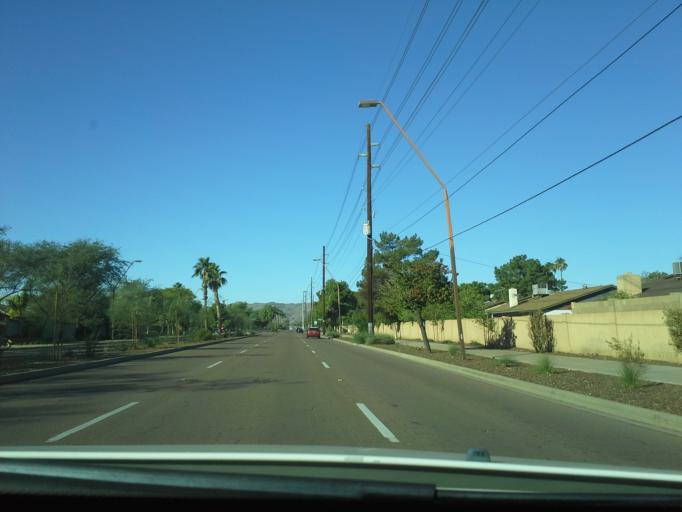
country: US
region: Arizona
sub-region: Maricopa County
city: Guadalupe
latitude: 33.3493
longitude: -111.9348
